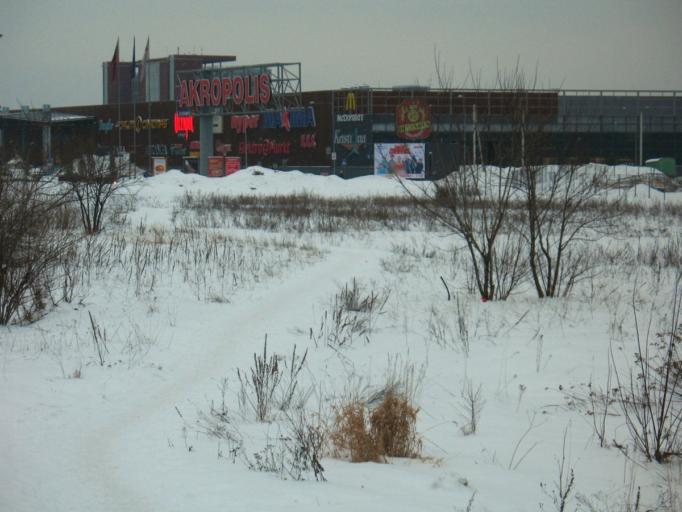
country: LT
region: Vilnius County
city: Seskine
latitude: 54.7102
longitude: 25.2561
